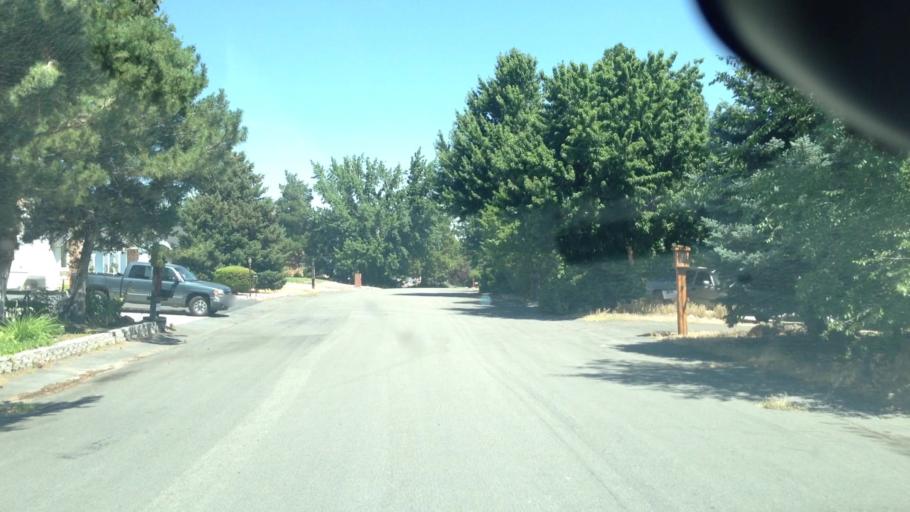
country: US
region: Nevada
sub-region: Washoe County
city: Sparks
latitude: 39.4196
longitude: -119.7689
